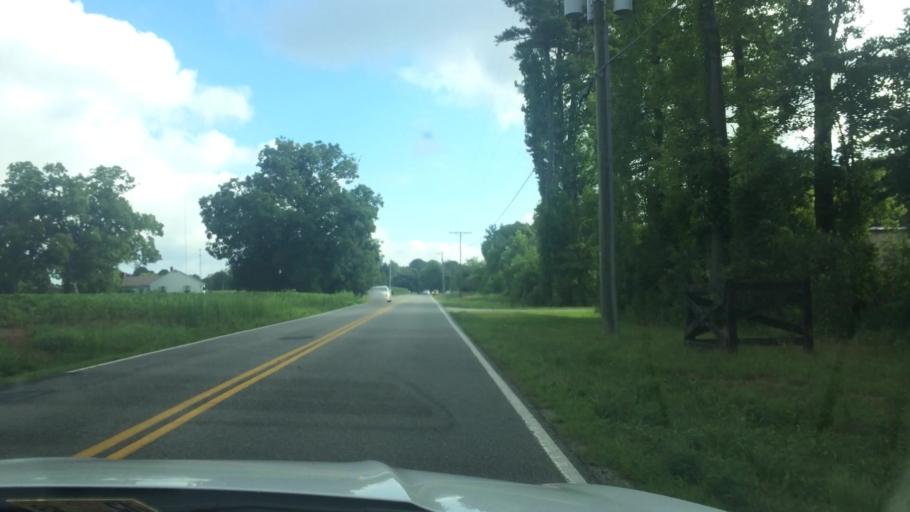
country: US
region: Virginia
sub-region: Gloucester County
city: Gloucester Courthouse
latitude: 37.4813
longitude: -76.4444
